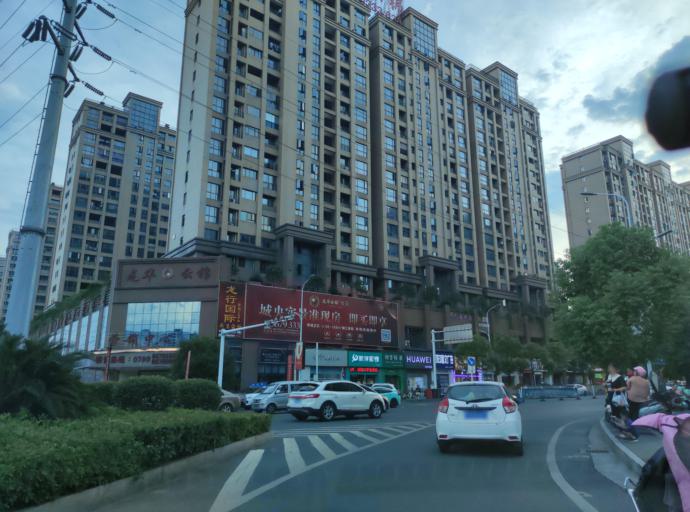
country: CN
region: Jiangxi Sheng
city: Pingxiang
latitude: 27.6334
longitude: 113.8689
